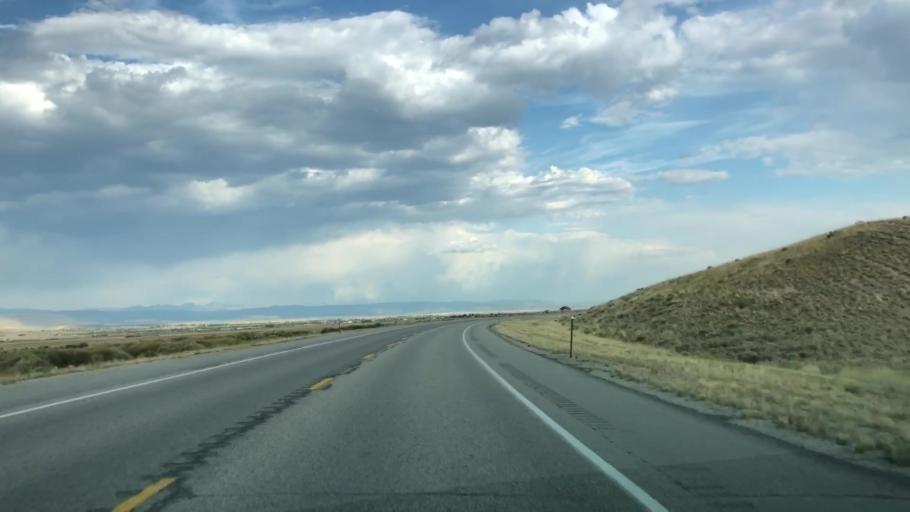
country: US
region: Wyoming
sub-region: Sublette County
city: Pinedale
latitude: 42.8746
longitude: -109.9398
